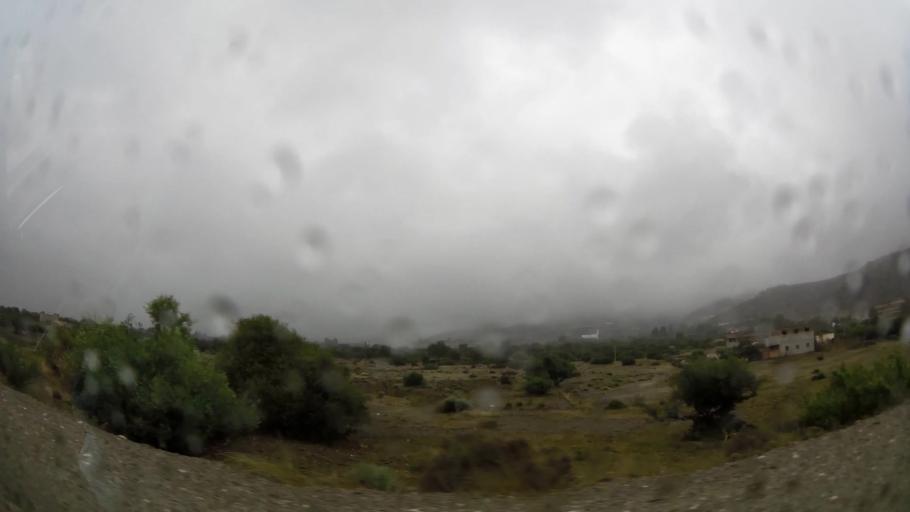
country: MA
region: Taza-Al Hoceima-Taounate
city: Imzourene
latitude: 35.1377
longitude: -3.7839
